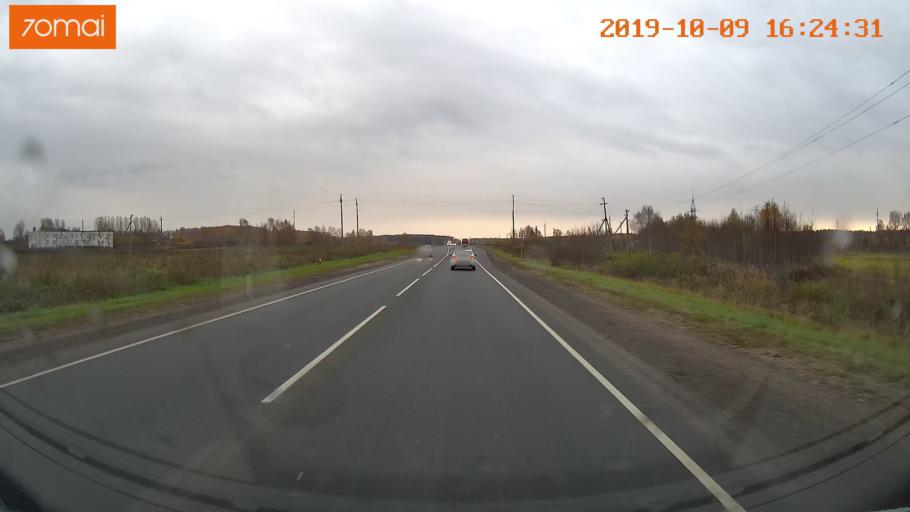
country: RU
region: Kostroma
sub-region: Kostromskoy Rayon
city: Kostroma
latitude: 57.6513
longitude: 40.9116
